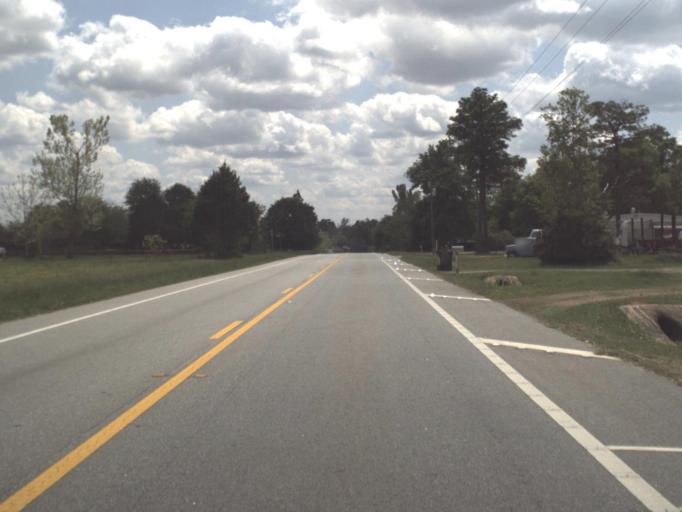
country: US
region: Alabama
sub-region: Escambia County
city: Atmore
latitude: 30.9536
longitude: -87.4866
